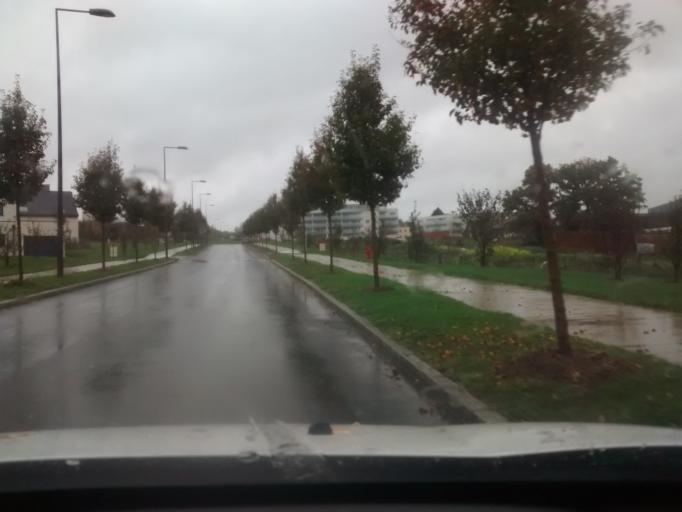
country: FR
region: Brittany
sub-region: Departement d'Ille-et-Vilaine
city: Fouillard
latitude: 48.1497
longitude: -1.5784
